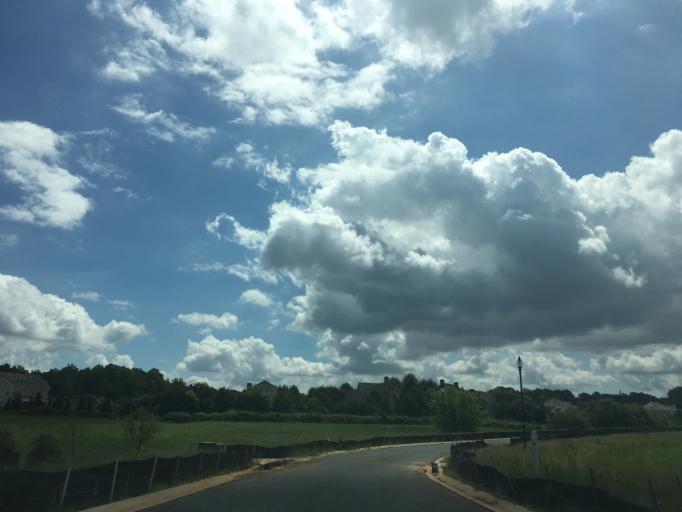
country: US
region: Georgia
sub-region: Fulton County
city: Roswell
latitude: 34.0981
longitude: -84.3773
